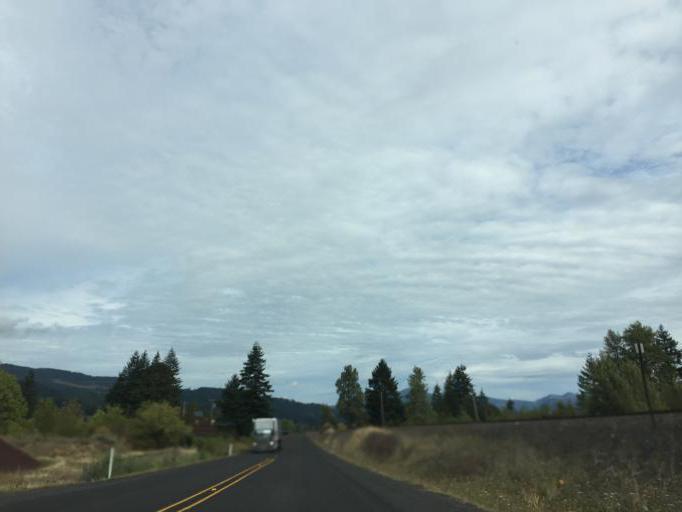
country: US
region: Oregon
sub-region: Hood River County
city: Cascade Locks
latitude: 45.6832
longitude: -121.9000
